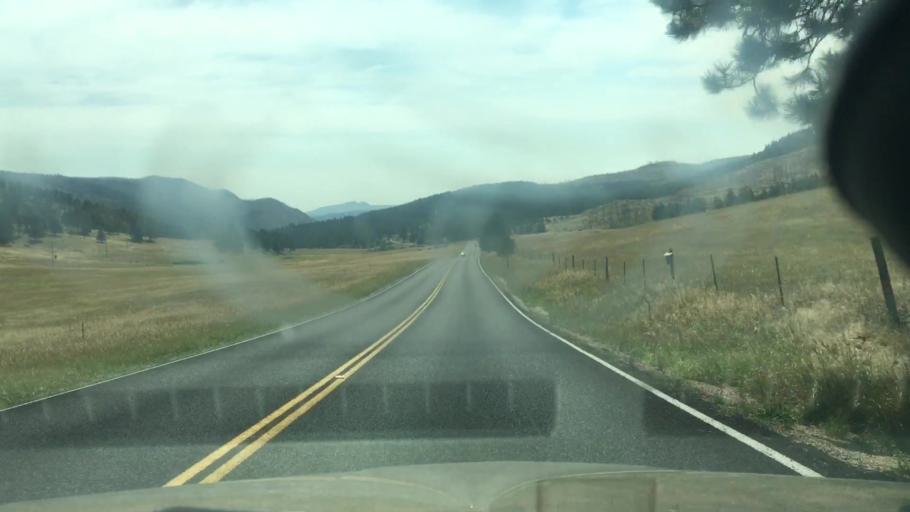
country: US
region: Colorado
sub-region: Larimer County
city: Laporte
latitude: 40.6170
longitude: -105.3566
